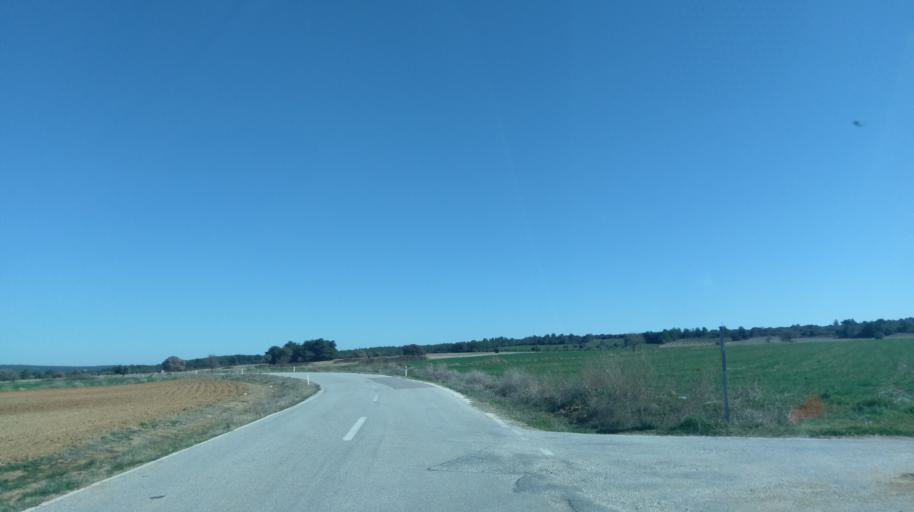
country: TR
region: Canakkale
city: Intepe
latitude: 40.1066
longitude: 26.2384
